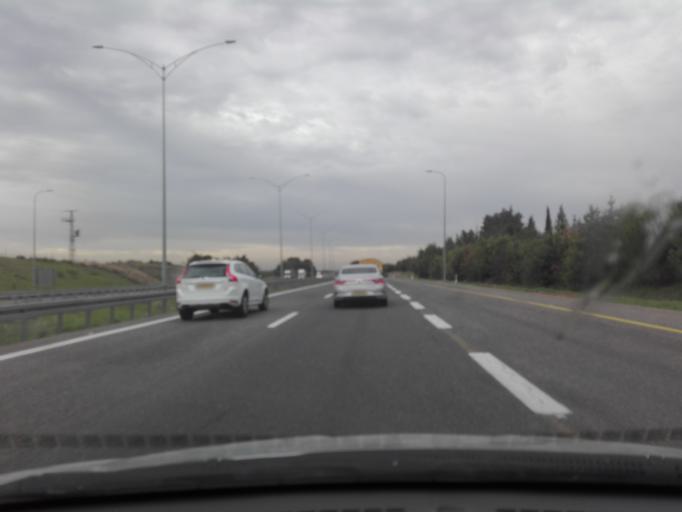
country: IL
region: Central District
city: Mazkeret Batya
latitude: 31.8778
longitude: 34.8771
